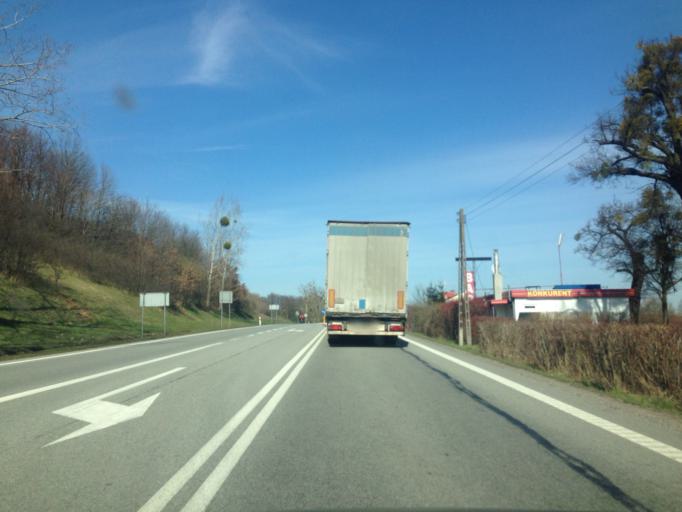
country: PL
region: Pomeranian Voivodeship
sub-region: Powiat starogardzki
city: Smetowo Graniczne
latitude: 53.7111
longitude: 18.7228
